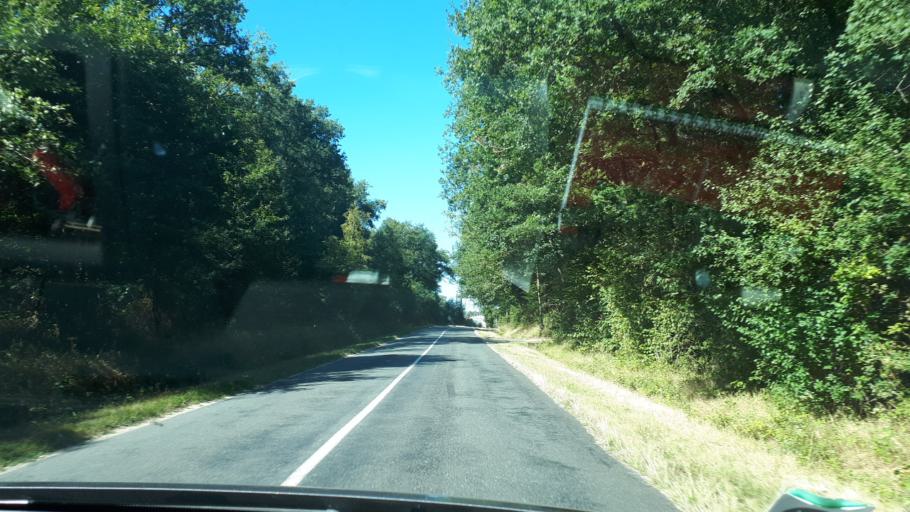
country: FR
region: Centre
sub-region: Departement du Loiret
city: Cerdon
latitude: 47.6376
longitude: 2.3806
